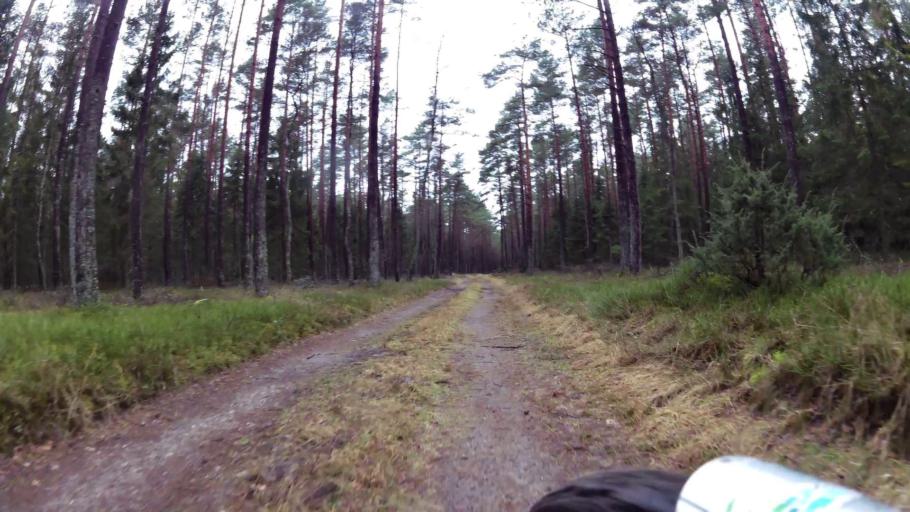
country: PL
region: Pomeranian Voivodeship
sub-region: Powiat bytowski
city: Borzytuchom
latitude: 54.2574
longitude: 17.3759
